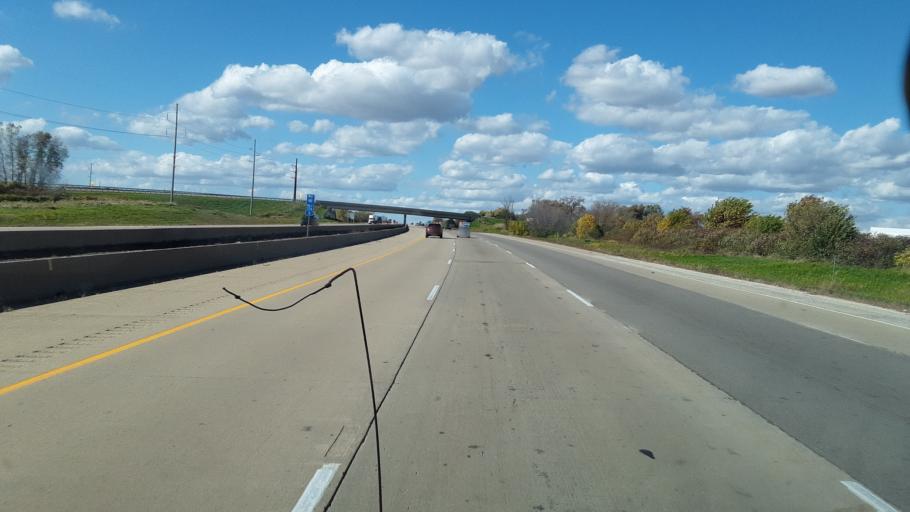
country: US
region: Wisconsin
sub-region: Dane County
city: De Forest
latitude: 43.2554
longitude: -89.3823
